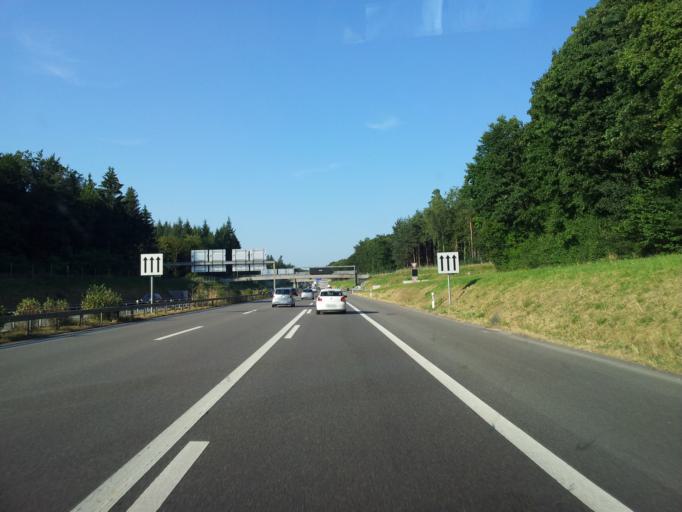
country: CH
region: Bern
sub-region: Bern-Mittelland District
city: Koniz
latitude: 46.9547
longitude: 7.4164
